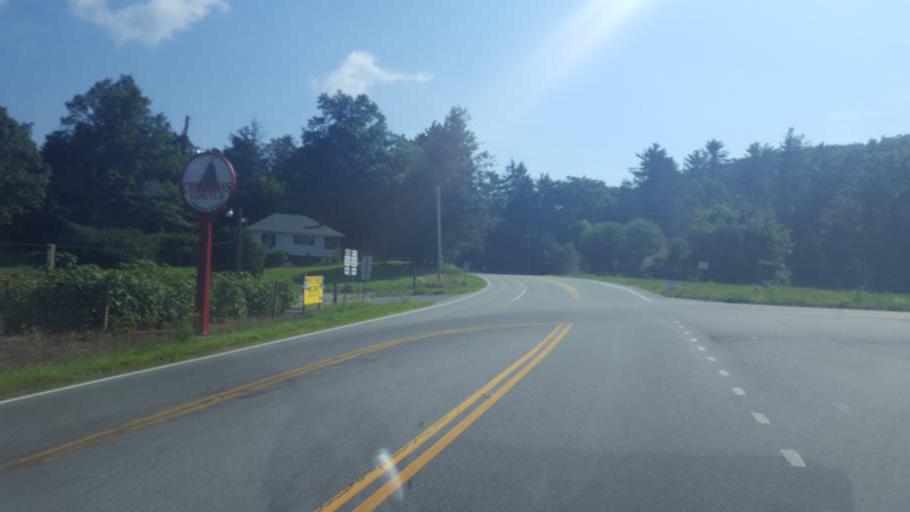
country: US
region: North Carolina
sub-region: Avery County
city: Newland
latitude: 36.0285
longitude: -81.8922
